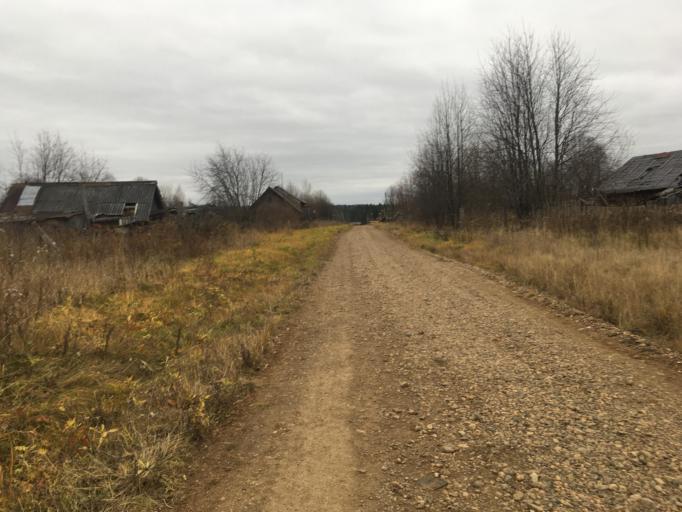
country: RU
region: Perm
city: Komarikhinskiy
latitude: 58.0922
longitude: 57.1122
